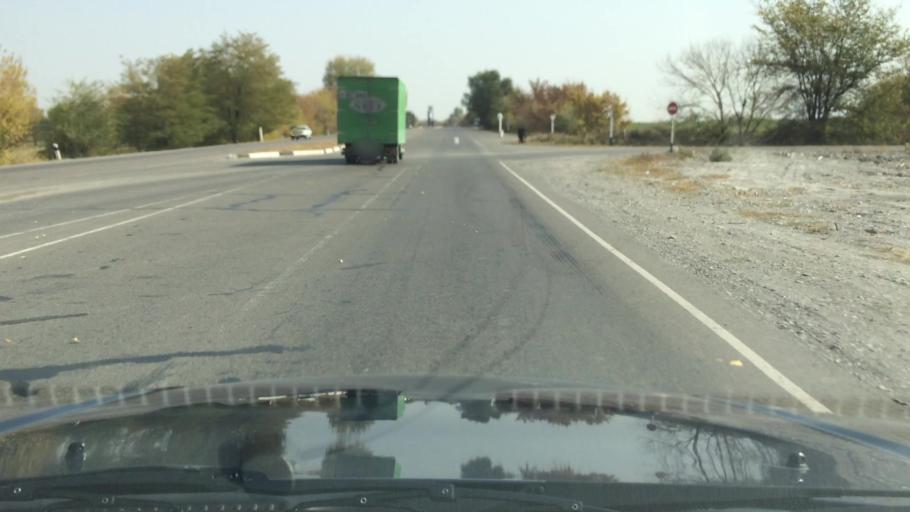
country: KG
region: Chuy
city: Lebedinovka
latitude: 42.9224
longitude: 74.7509
